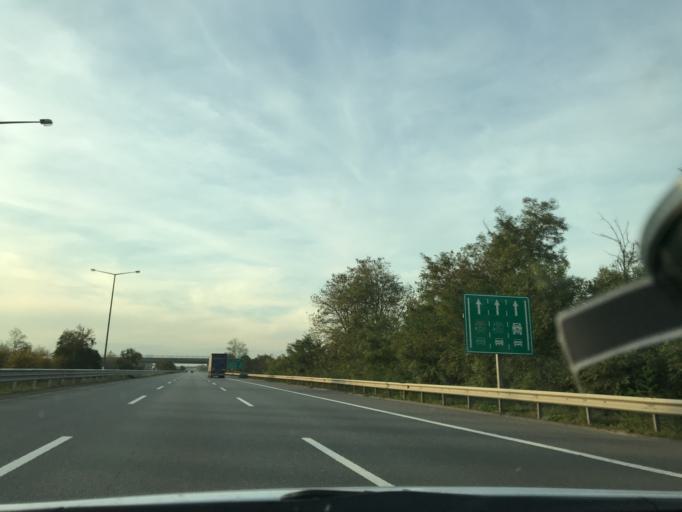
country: TR
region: Duzce
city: Cilimli
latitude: 40.8355
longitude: 31.0346
